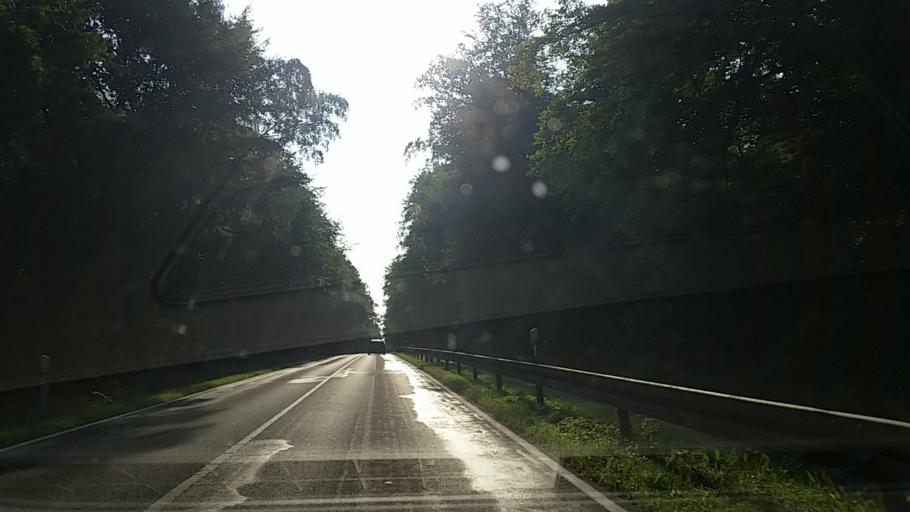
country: DE
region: Mecklenburg-Vorpommern
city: Wittenburg
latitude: 53.4850
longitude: 11.1105
